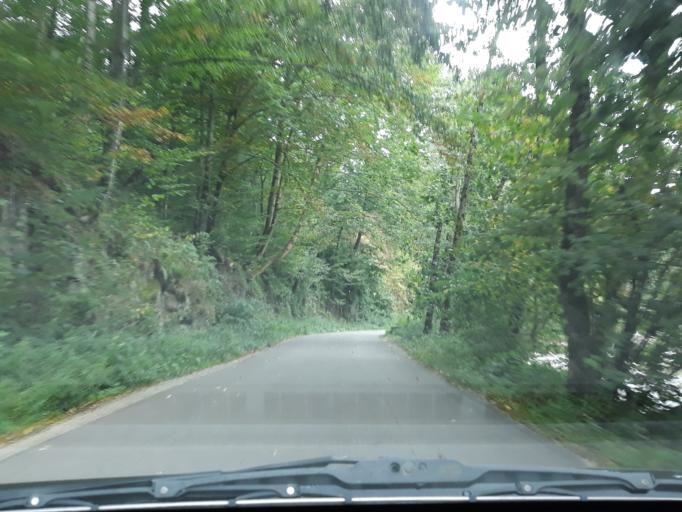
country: RO
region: Bihor
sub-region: Comuna Pietroasa
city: Pietroasa
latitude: 46.5885
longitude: 22.5934
